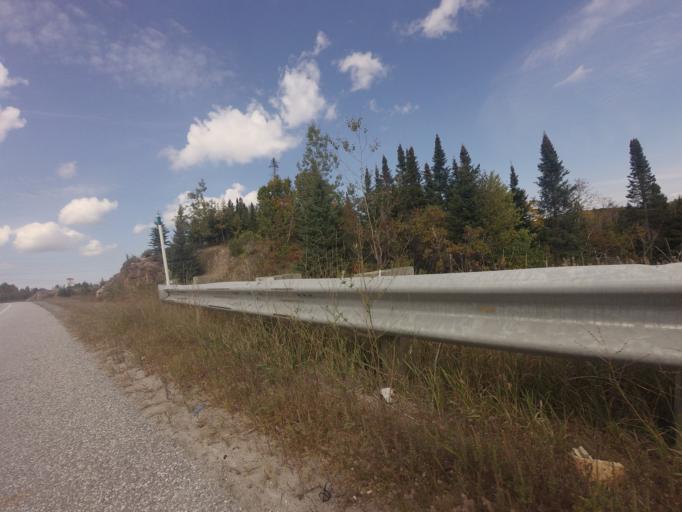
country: CA
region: Quebec
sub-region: Laurentides
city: Mont-Laurier
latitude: 46.5598
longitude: -75.6499
